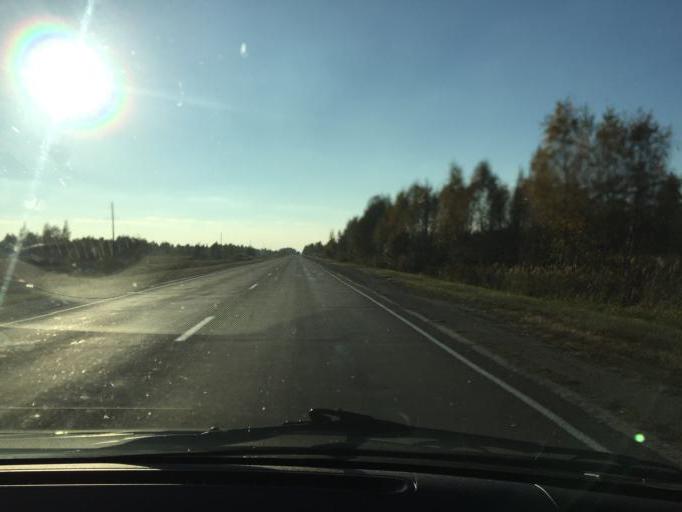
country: BY
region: Brest
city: Horad Luninyets
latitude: 52.3156
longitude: 26.5660
